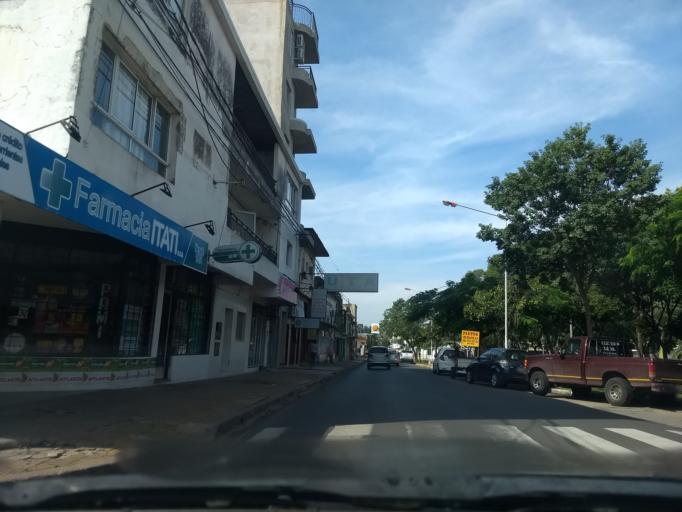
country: AR
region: Corrientes
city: Corrientes
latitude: -27.4700
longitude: -58.8229
